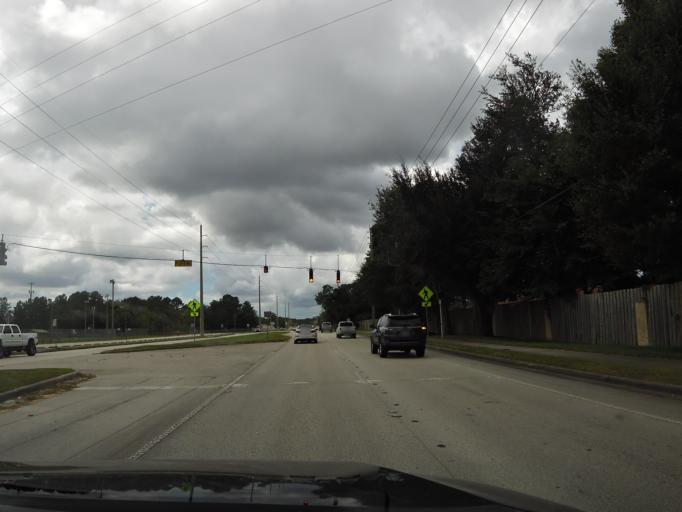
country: US
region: Florida
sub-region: Clay County
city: Lakeside
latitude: 30.1004
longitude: -81.7633
